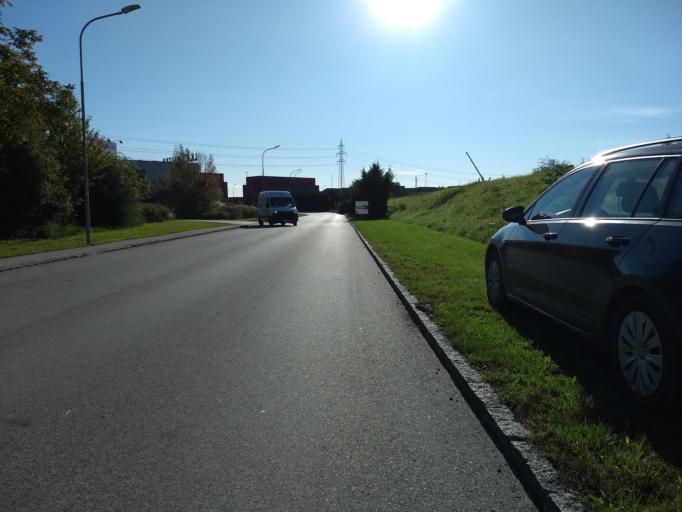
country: AT
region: Lower Austria
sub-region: Politischer Bezirk Modling
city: Neu-Guntramsdorf
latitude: 48.0665
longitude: 16.3343
